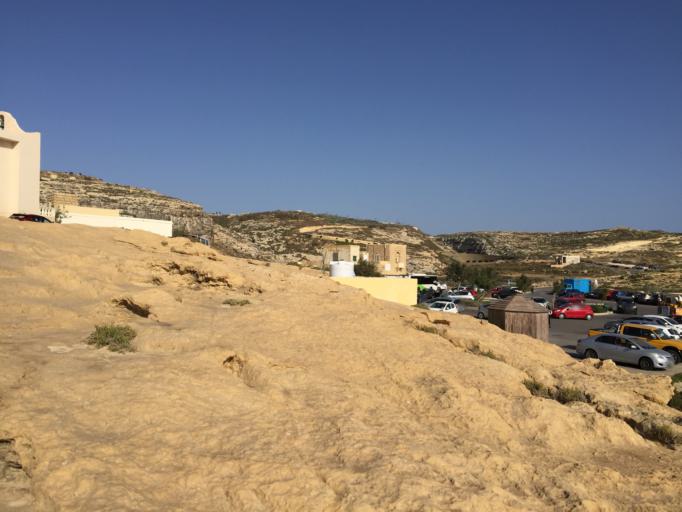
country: MT
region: Saint Lawrence
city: San Lawrenz
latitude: 36.0527
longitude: 14.1895
